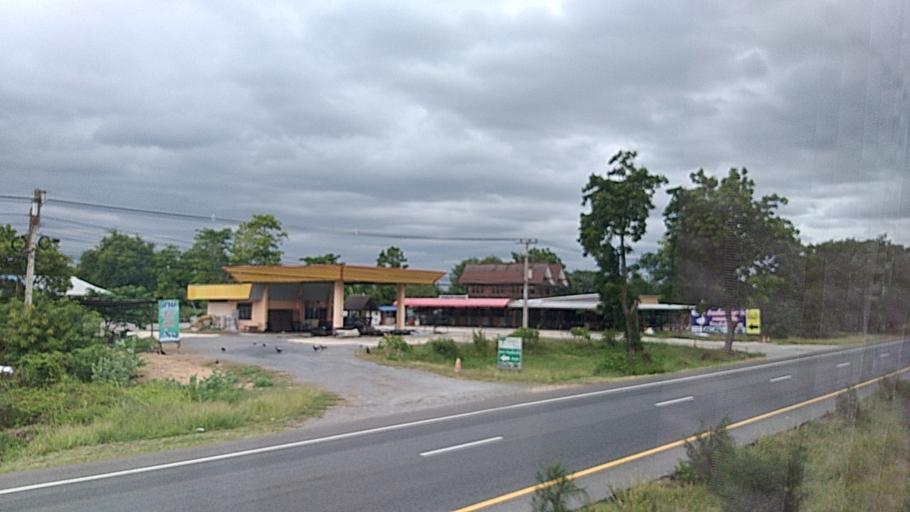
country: TH
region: Khon Kaen
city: Non Sila
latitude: 16.0092
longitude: 102.7045
